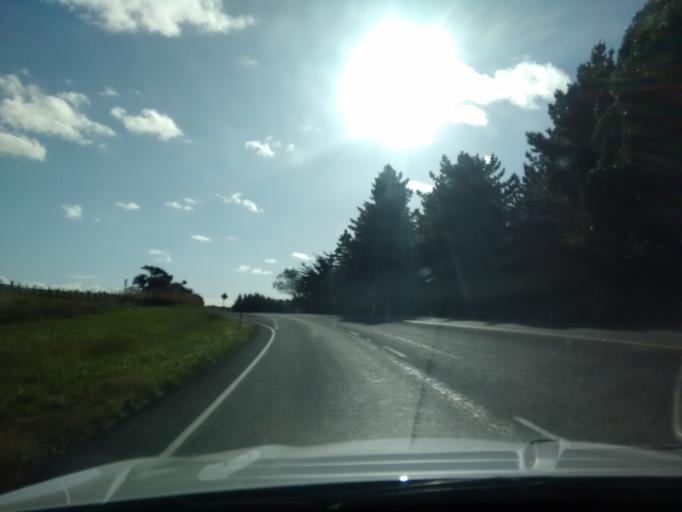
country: NZ
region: Manawatu-Wanganui
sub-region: Wanganui District
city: Wanganui
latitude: -39.8369
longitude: 174.9155
